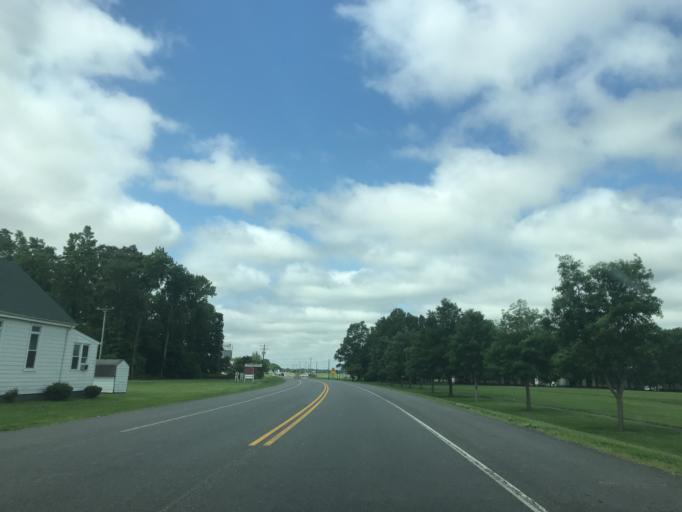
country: US
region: Maryland
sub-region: Caroline County
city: Ridgely
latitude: 38.9406
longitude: -75.8851
